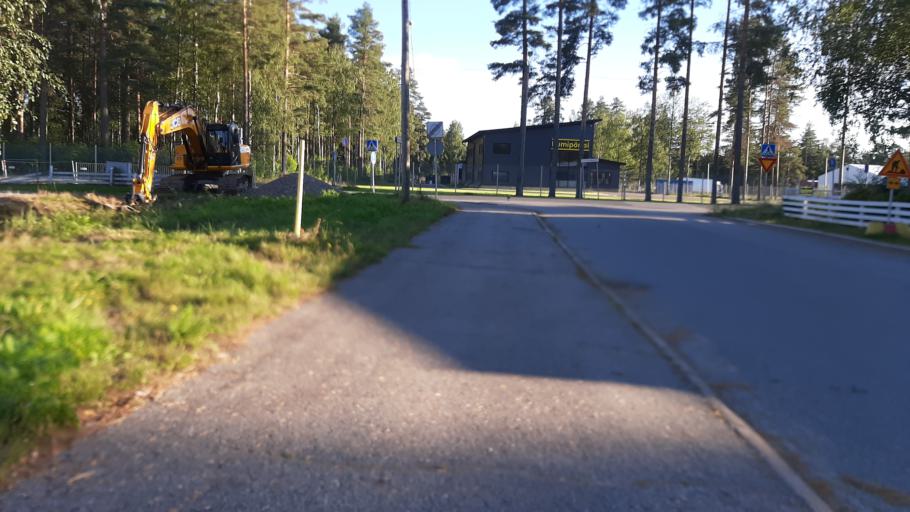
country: FI
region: North Karelia
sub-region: Joensuu
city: Joensuu
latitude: 62.6187
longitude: 29.7459
